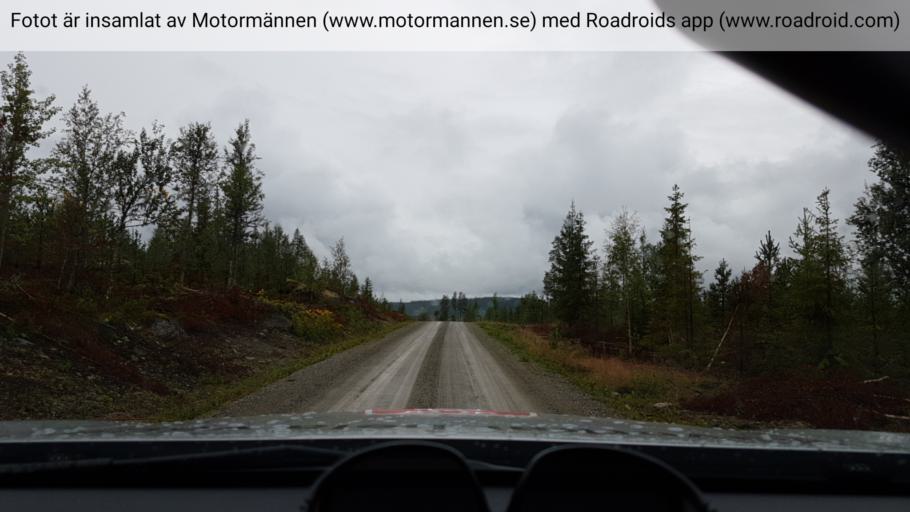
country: SE
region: Vaesterbotten
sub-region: Storumans Kommun
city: Storuman
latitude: 64.8362
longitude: 17.4043
